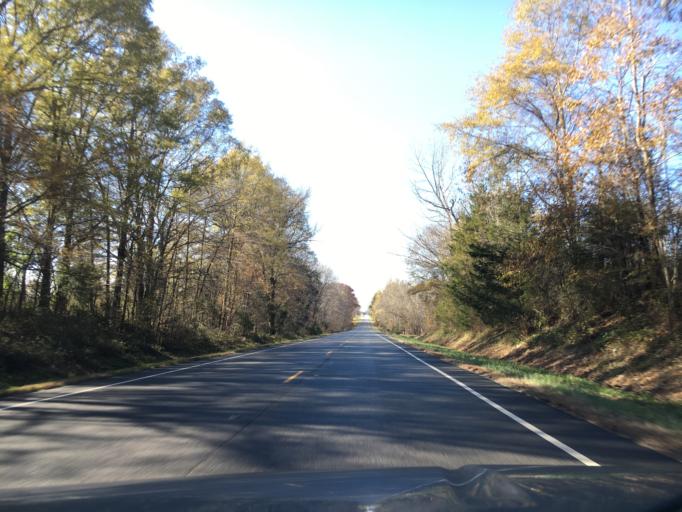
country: US
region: Virginia
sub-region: Cumberland County
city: Cumberland
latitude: 37.5123
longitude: -78.2224
